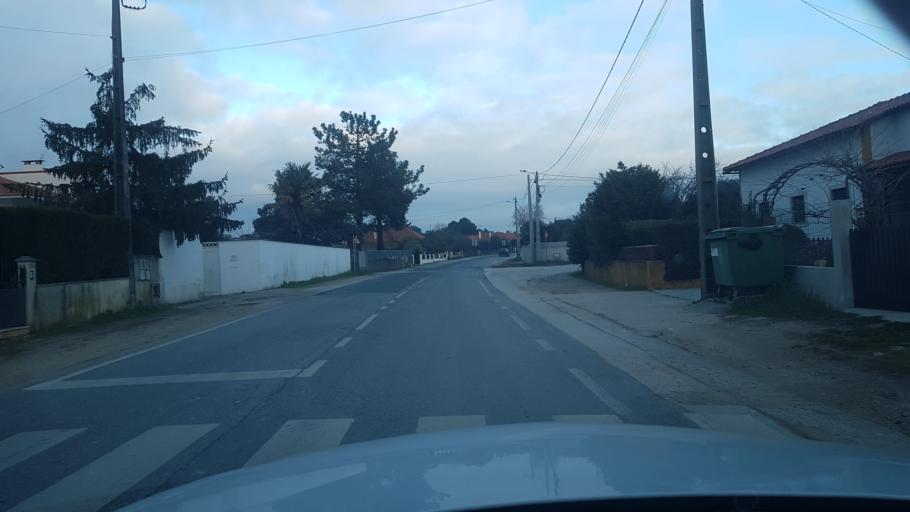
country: PT
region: Santarem
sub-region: Ourem
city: Fatima
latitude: 39.5965
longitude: -8.6534
